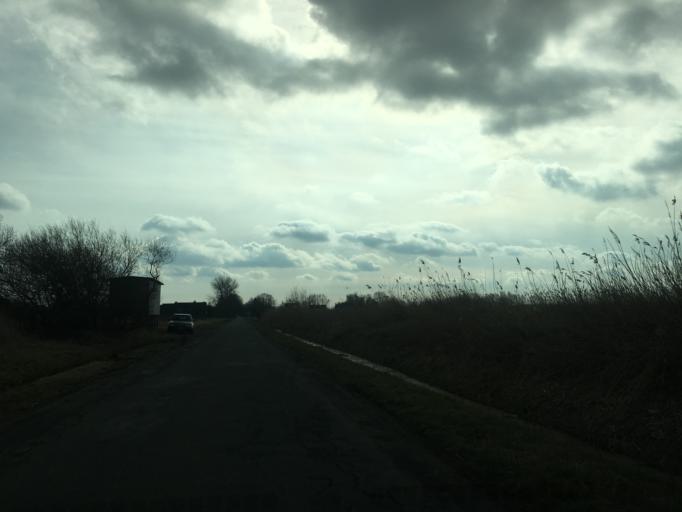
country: DE
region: North Rhine-Westphalia
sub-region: Regierungsbezirk Munster
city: Muenster
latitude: 52.0332
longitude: 7.6524
